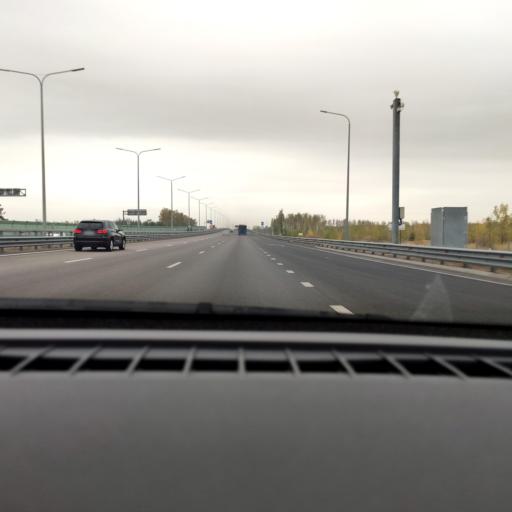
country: RU
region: Voronezj
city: Somovo
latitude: 51.7409
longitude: 39.3080
